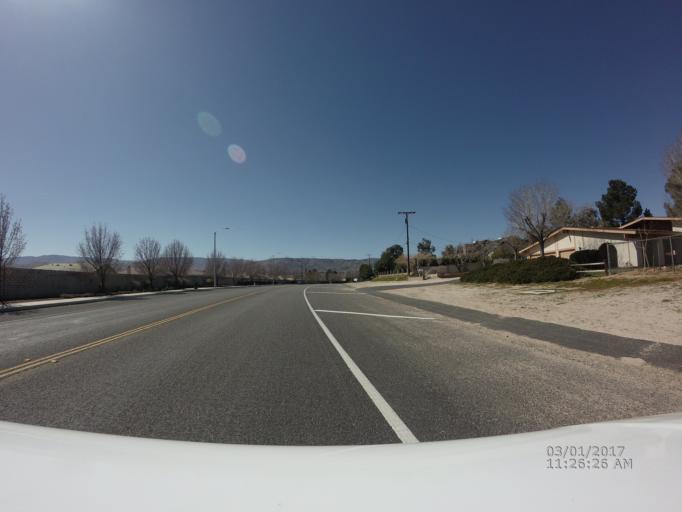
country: US
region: California
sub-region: Los Angeles County
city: Quartz Hill
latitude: 34.6452
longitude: -118.2080
